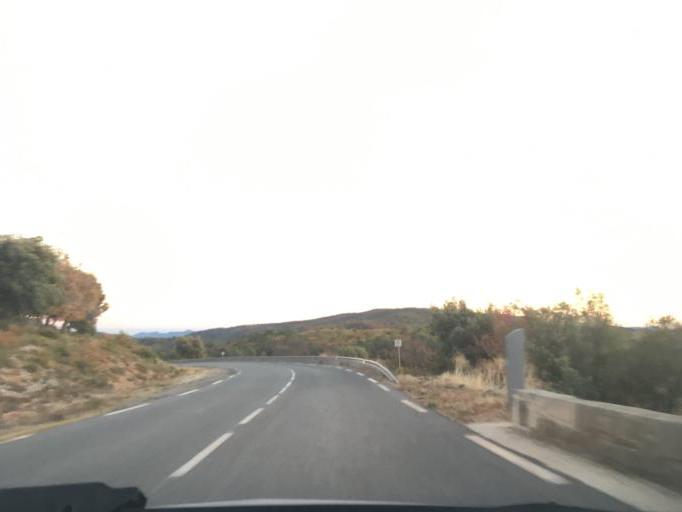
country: FR
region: Provence-Alpes-Cote d'Azur
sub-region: Departement du Var
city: Montferrat
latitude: 43.6351
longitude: 6.4801
